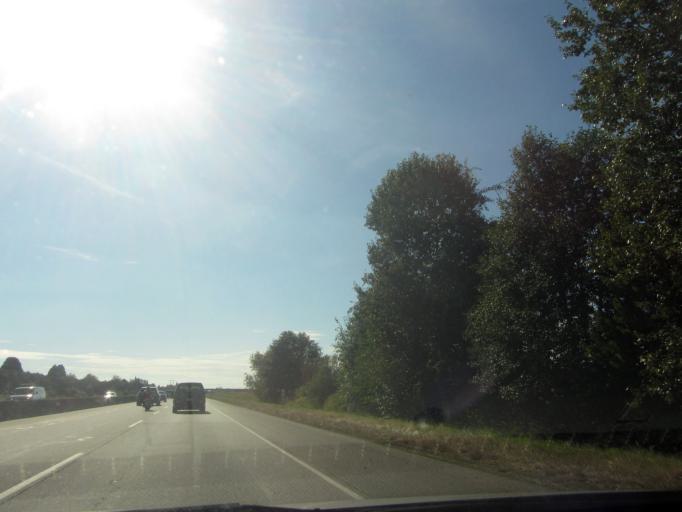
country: CA
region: British Columbia
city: Ladner
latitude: 49.1773
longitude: -123.0339
